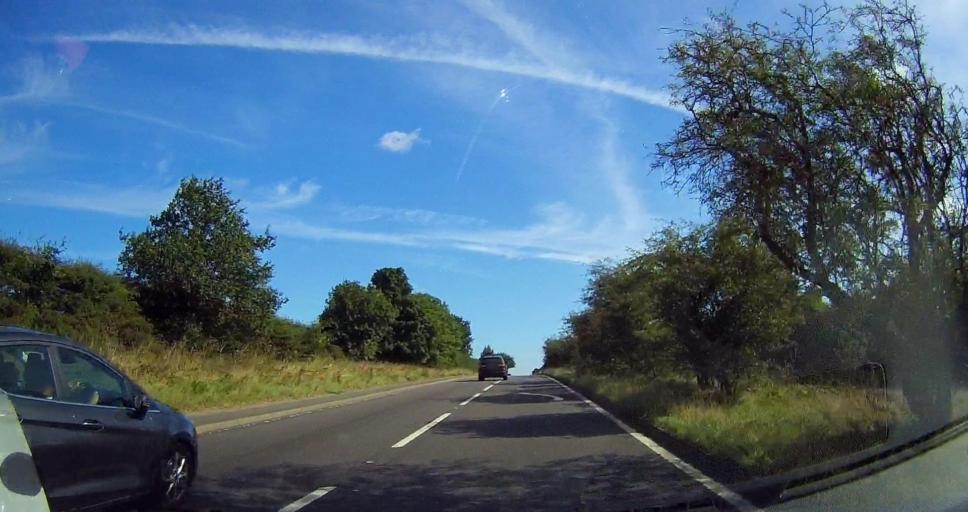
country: GB
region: England
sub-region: Staffordshire
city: Chasetown
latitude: 52.6562
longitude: -1.8950
